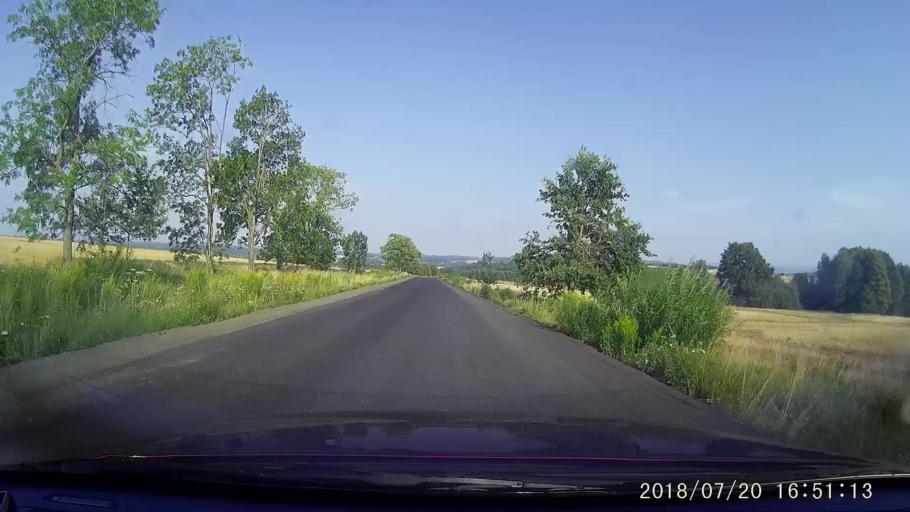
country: PL
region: Lower Silesian Voivodeship
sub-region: Powiat lubanski
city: Lesna
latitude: 51.0388
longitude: 15.2172
